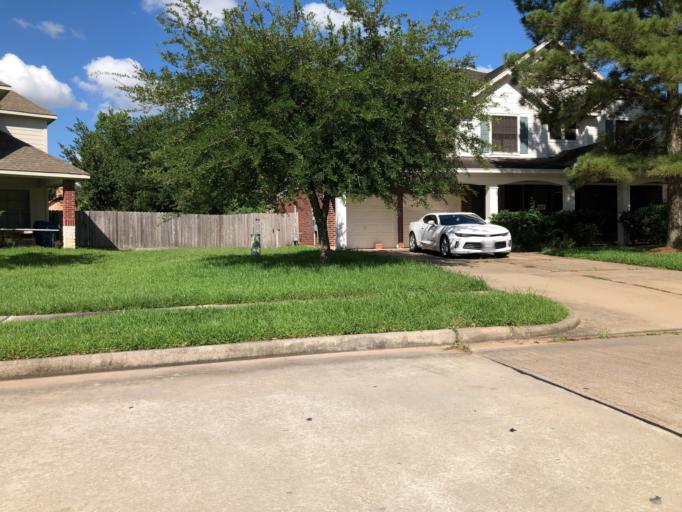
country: US
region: Texas
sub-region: Harris County
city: Katy
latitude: 29.8079
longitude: -95.8276
